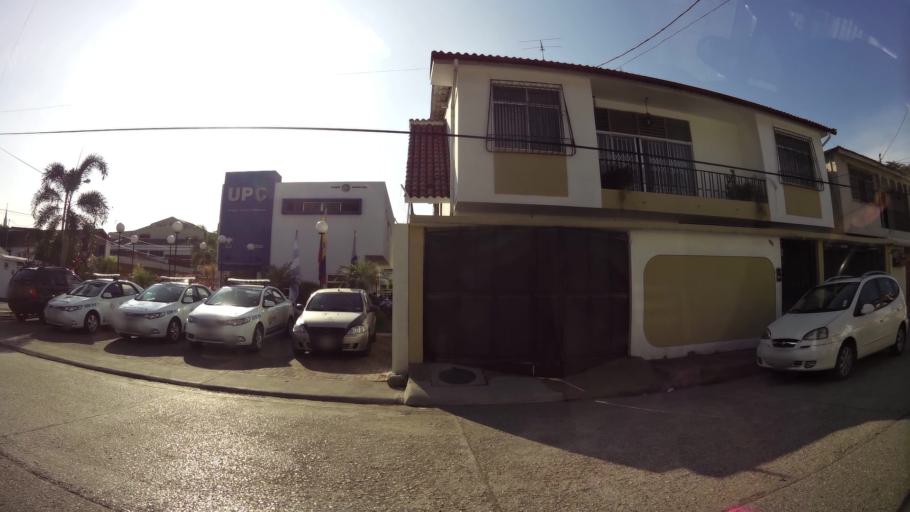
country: EC
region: Guayas
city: Guayaquil
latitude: -2.1599
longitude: -79.9072
